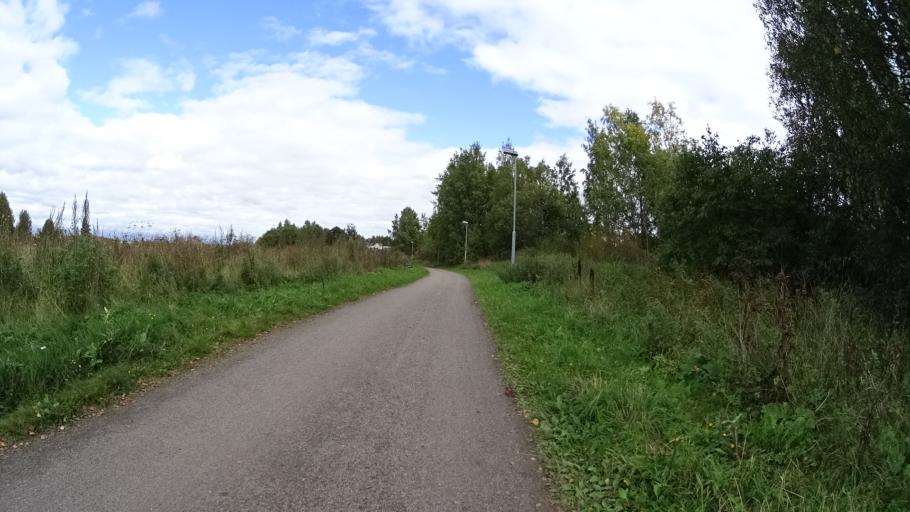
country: FI
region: Uusimaa
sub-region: Helsinki
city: Vantaa
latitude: 60.2487
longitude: 25.0273
